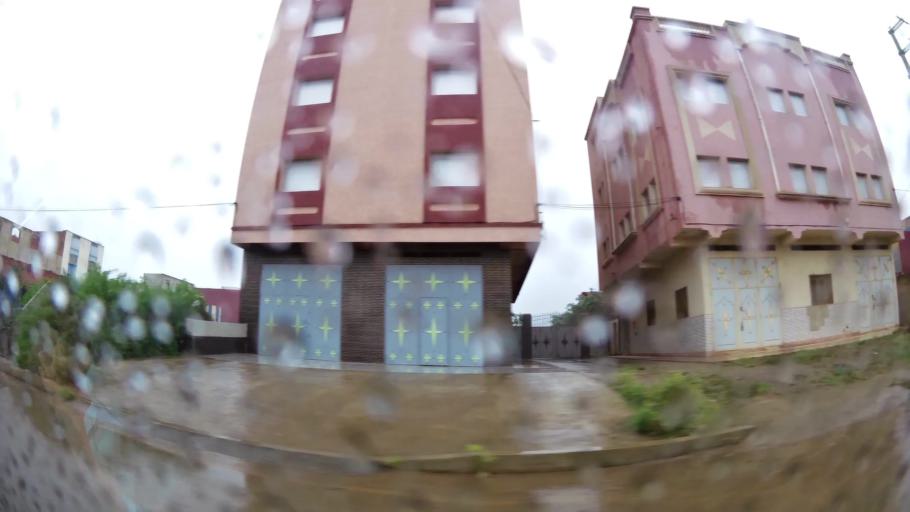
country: MA
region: Oriental
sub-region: Nador
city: Boudinar
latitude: 35.1193
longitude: -3.6440
